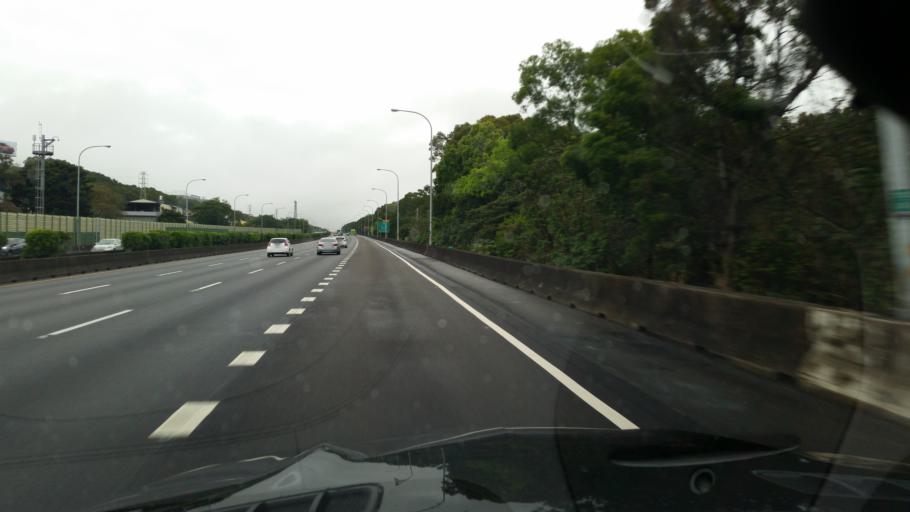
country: TW
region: Taiwan
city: Fengyuan
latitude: 24.3747
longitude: 120.7491
